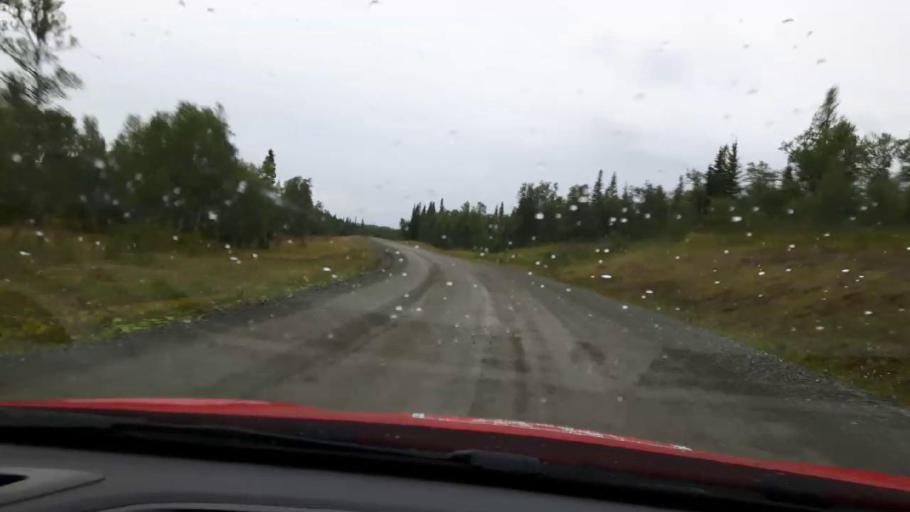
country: NO
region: Nord-Trondelag
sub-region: Meraker
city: Meraker
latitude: 63.5638
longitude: 12.2881
